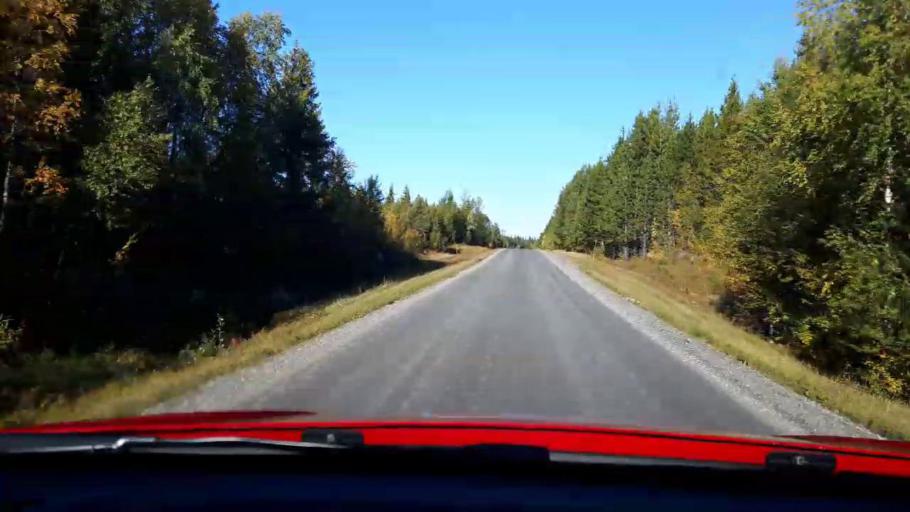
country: NO
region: Nord-Trondelag
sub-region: Lierne
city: Sandvika
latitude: 64.5277
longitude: 14.0531
